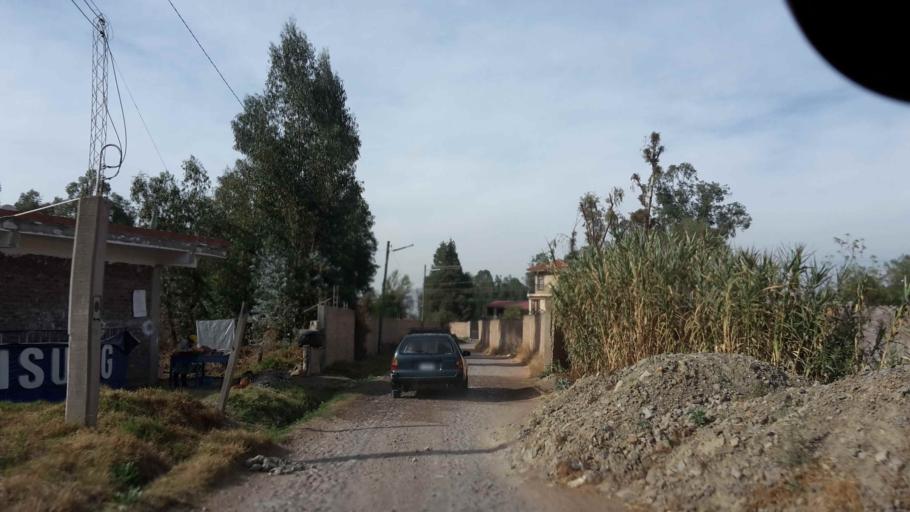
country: BO
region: Cochabamba
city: Cochabamba
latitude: -17.3619
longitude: -66.2208
